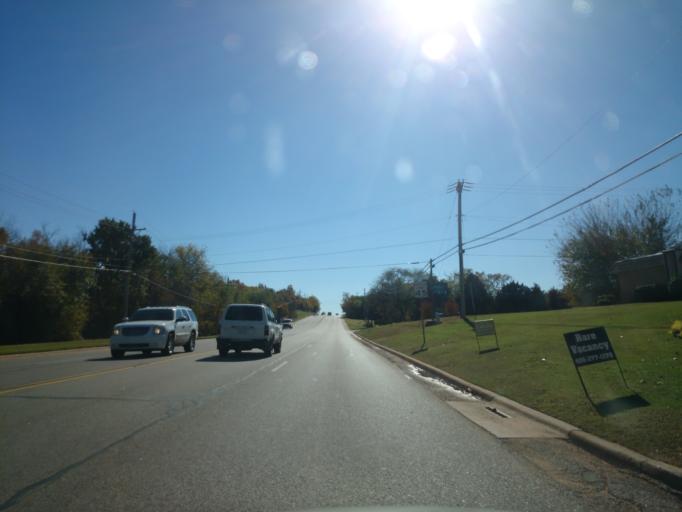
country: US
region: Oklahoma
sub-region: Payne County
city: Stillwater
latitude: 36.1589
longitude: -97.0698
